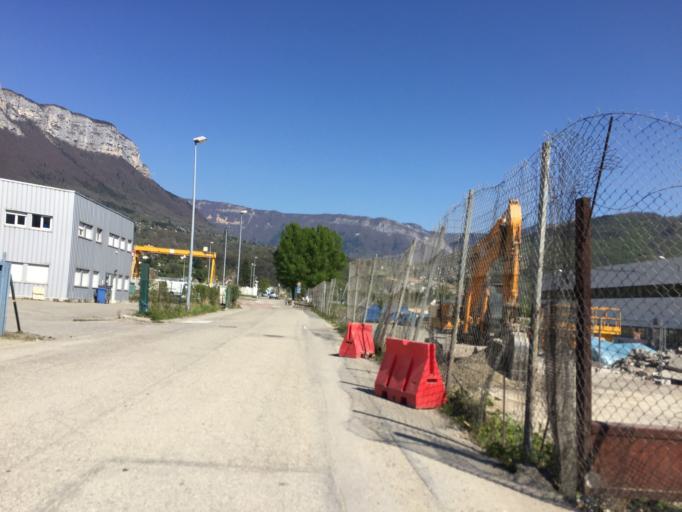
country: FR
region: Rhone-Alpes
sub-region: Departement de la Savoie
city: Saint-Alban-Leysse
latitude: 45.5741
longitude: 5.9607
